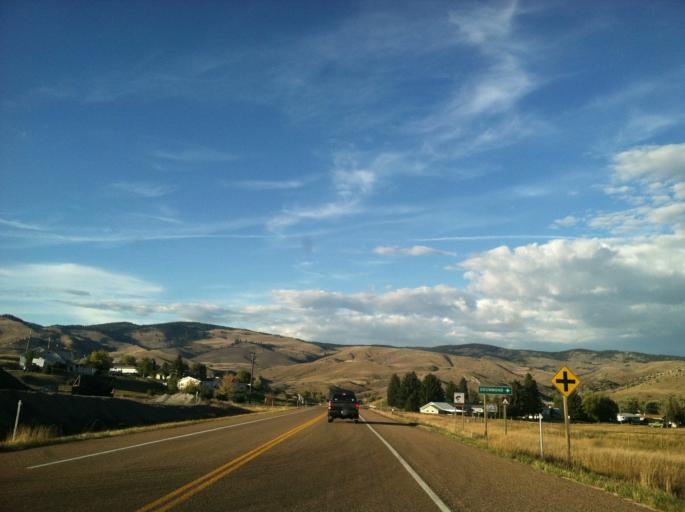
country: US
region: Montana
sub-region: Granite County
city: Philipsburg
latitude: 46.6579
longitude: -113.1587
